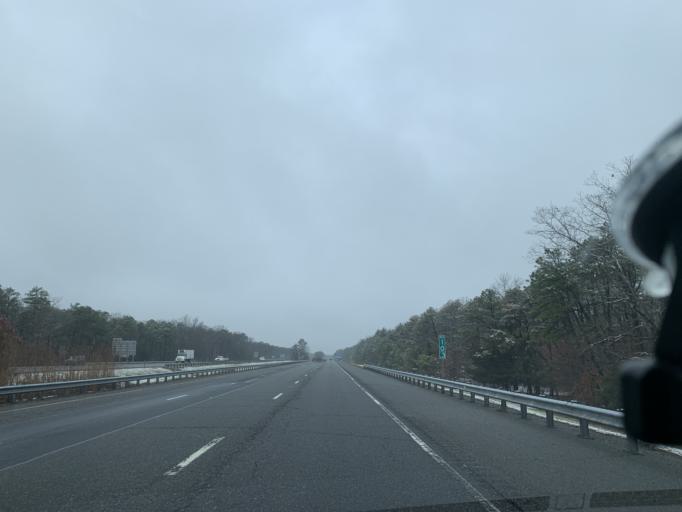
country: US
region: New Jersey
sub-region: Atlantic County
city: Pomona
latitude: 39.4394
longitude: -74.5992
